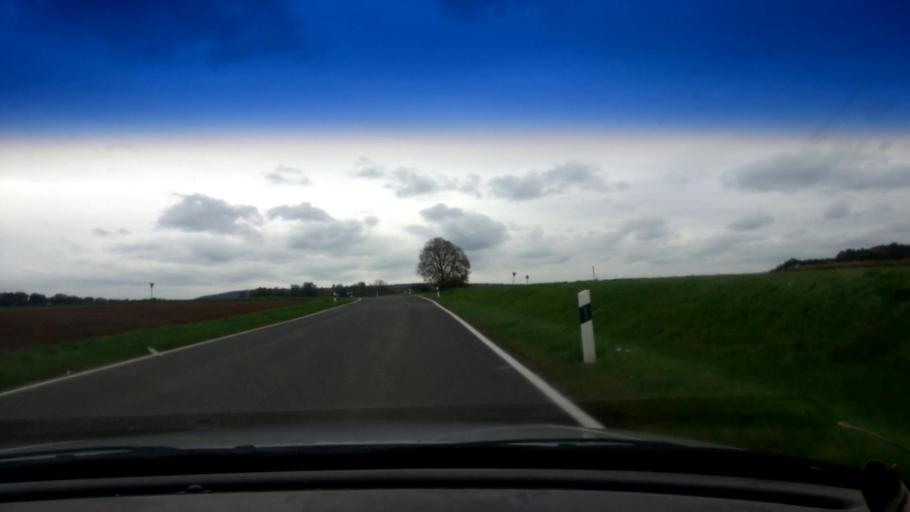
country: DE
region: Bavaria
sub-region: Upper Franconia
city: Gerach
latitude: 50.0253
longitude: 10.8165
